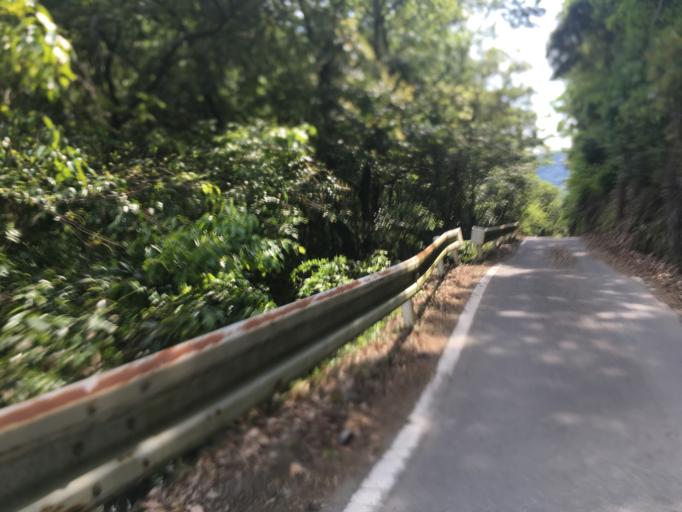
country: JP
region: Kyoto
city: Kameoka
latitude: 35.0284
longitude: 135.6487
